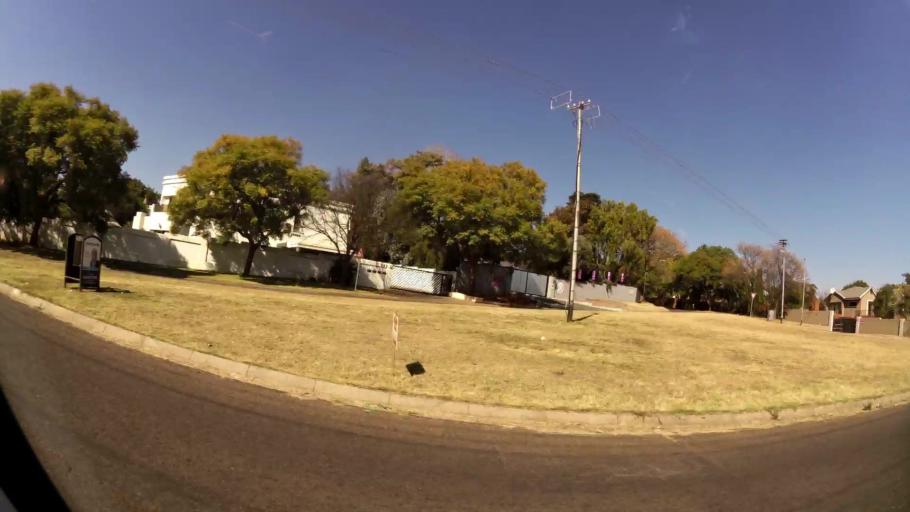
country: ZA
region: Gauteng
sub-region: City of Tshwane Metropolitan Municipality
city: Pretoria
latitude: -25.7960
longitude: 28.2402
